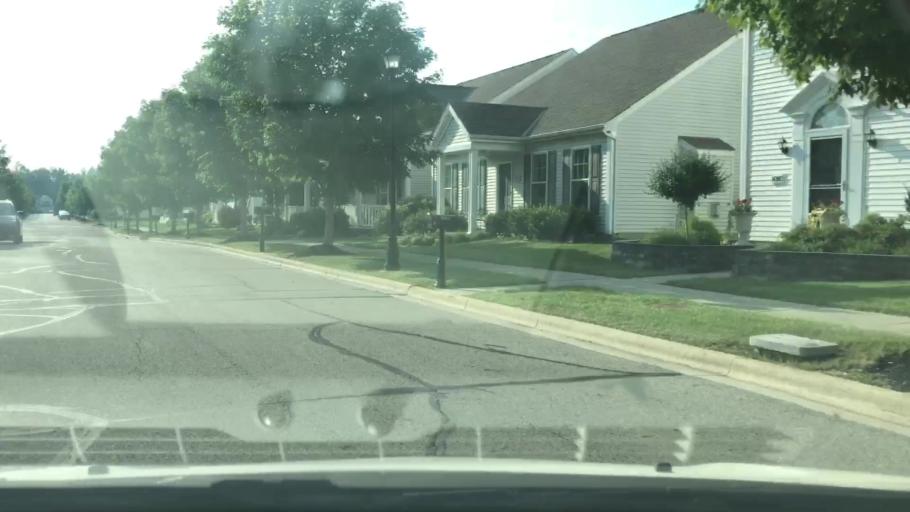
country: US
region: Ohio
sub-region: Franklin County
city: New Albany
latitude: 40.1029
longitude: -82.8543
